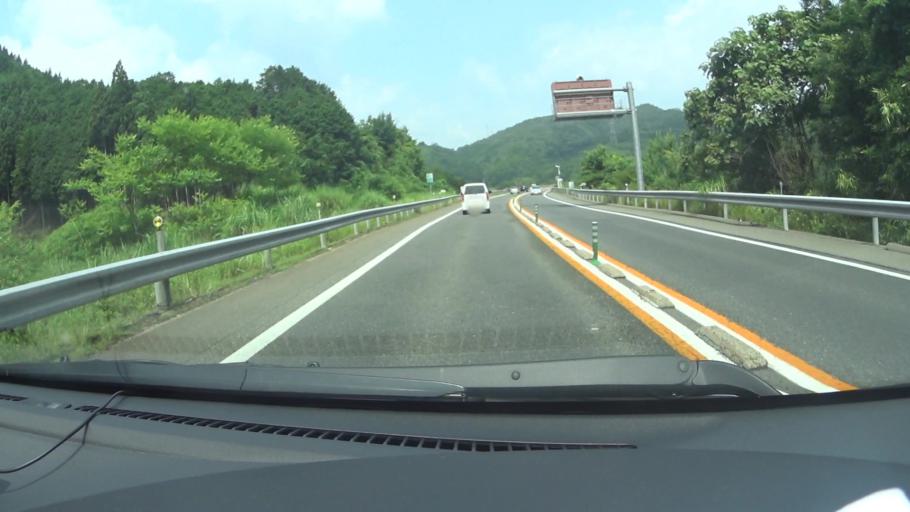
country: JP
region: Kyoto
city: Kameoka
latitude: 35.1277
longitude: 135.4626
